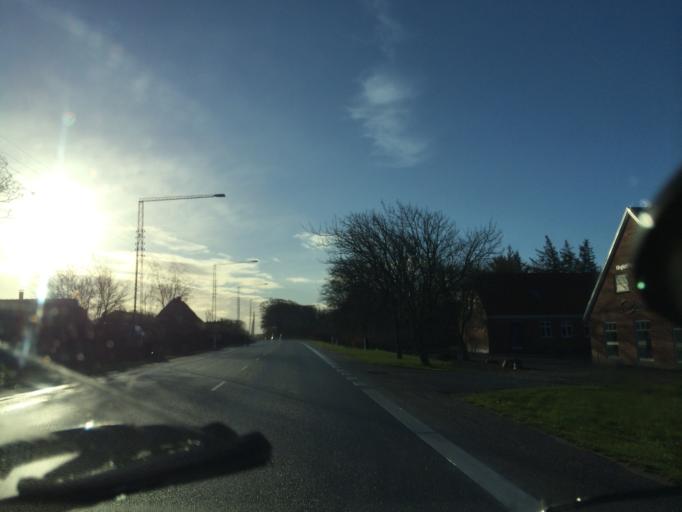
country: DK
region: Central Jutland
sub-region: Ringkobing-Skjern Kommune
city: Ringkobing
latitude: 56.1030
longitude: 8.2568
